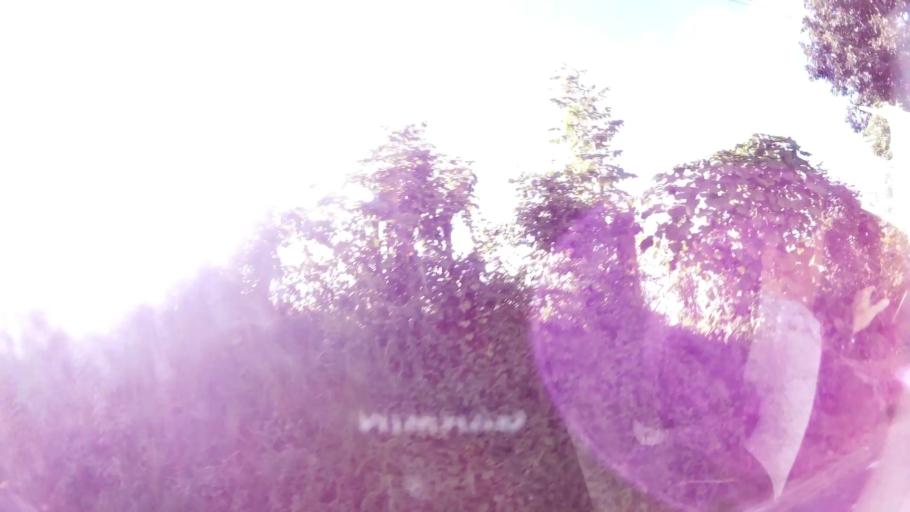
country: GT
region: Quiche
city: Chichicastenango
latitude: 14.9449
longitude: -91.1086
